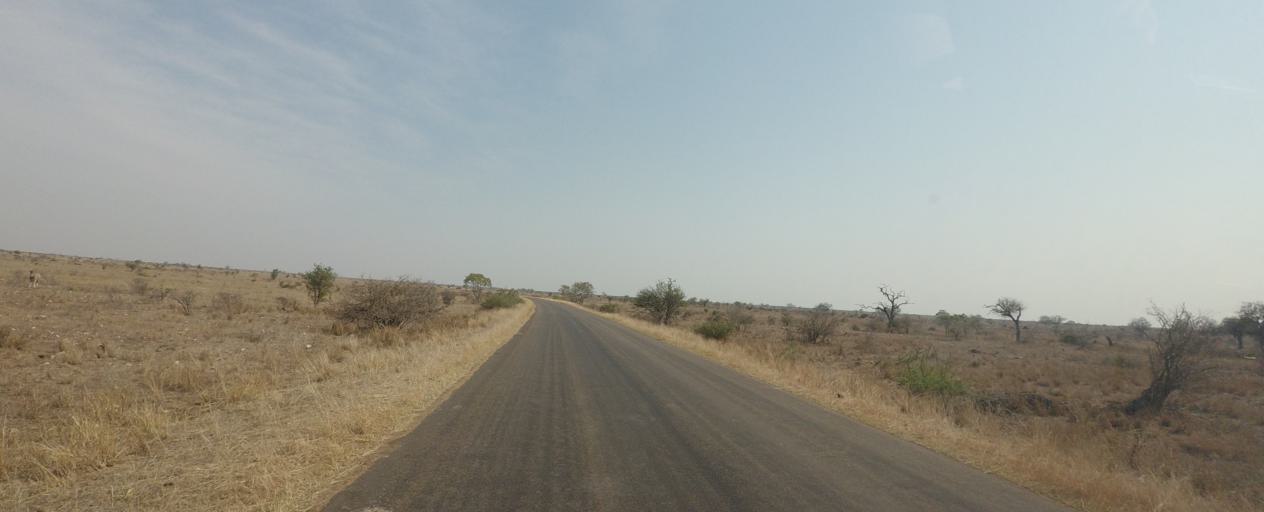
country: ZA
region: Limpopo
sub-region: Mopani District Municipality
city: Phalaborwa
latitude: -24.2791
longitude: 31.7394
